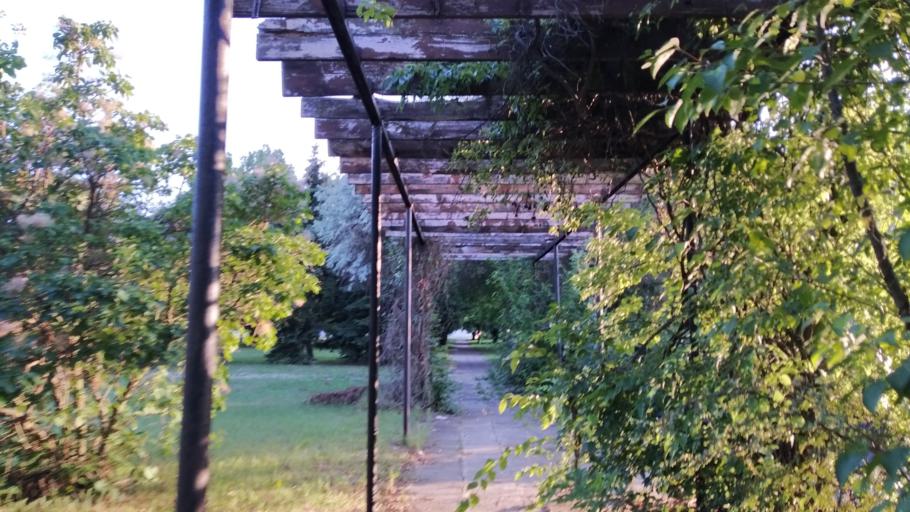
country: HU
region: Budapest
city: Budapest XIX. keruelet
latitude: 47.4249
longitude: 19.1340
